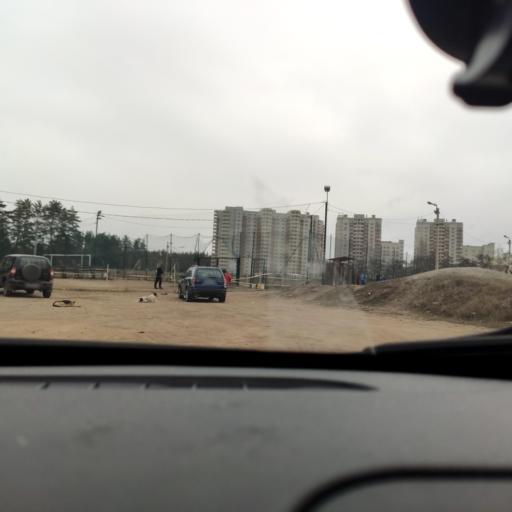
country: RU
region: Voronezj
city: Podgornoye
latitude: 51.7297
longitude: 39.1647
